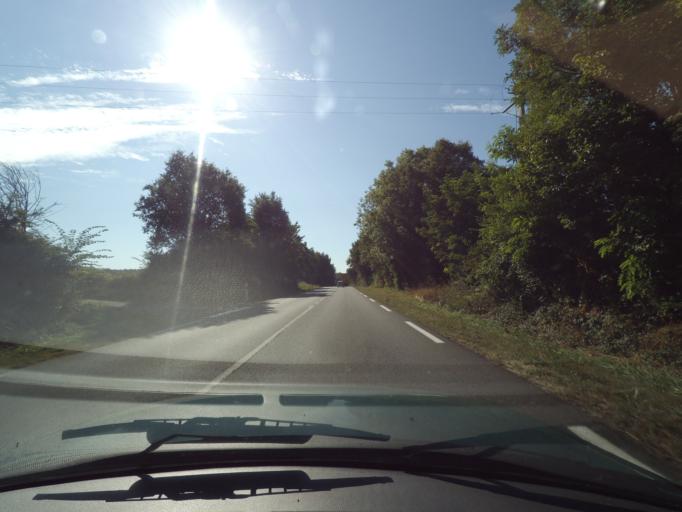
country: FR
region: Poitou-Charentes
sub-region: Departement de la Vienne
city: Terce
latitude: 46.4492
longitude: 0.5707
